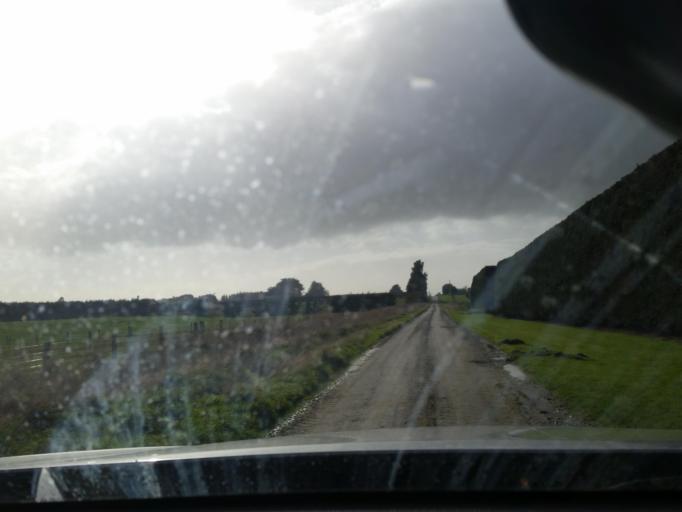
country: NZ
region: Southland
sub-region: Invercargill City
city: Invercargill
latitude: -46.3365
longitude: 168.3661
